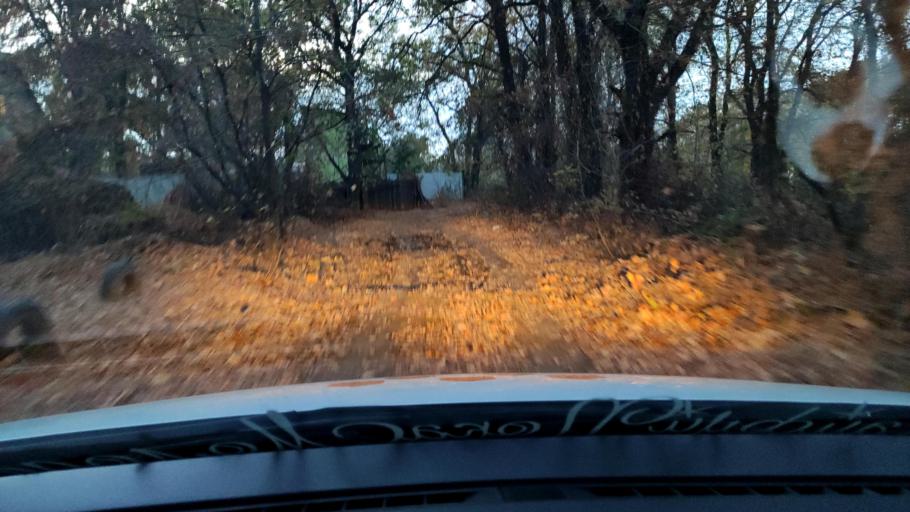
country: RU
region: Voronezj
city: Pridonskoy
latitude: 51.6627
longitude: 39.1184
